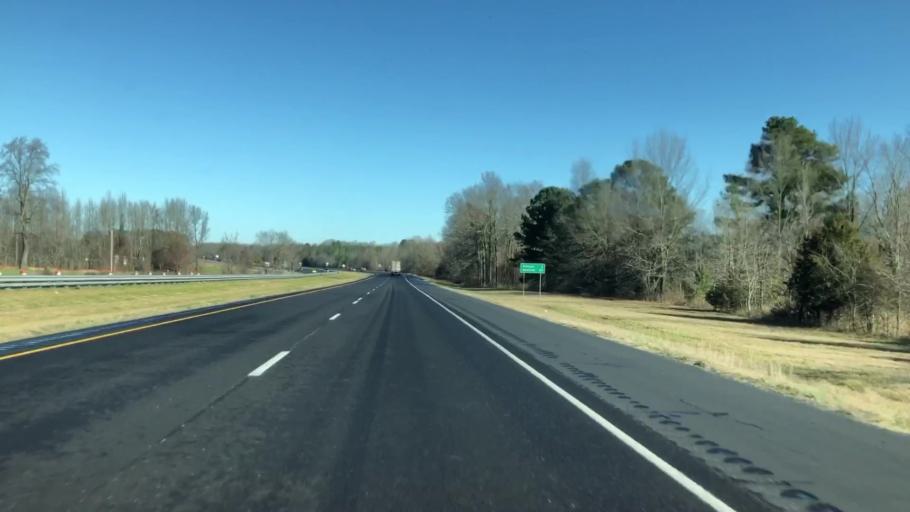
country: US
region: Alabama
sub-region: Limestone County
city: Ardmore
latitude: 34.9310
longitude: -86.8990
